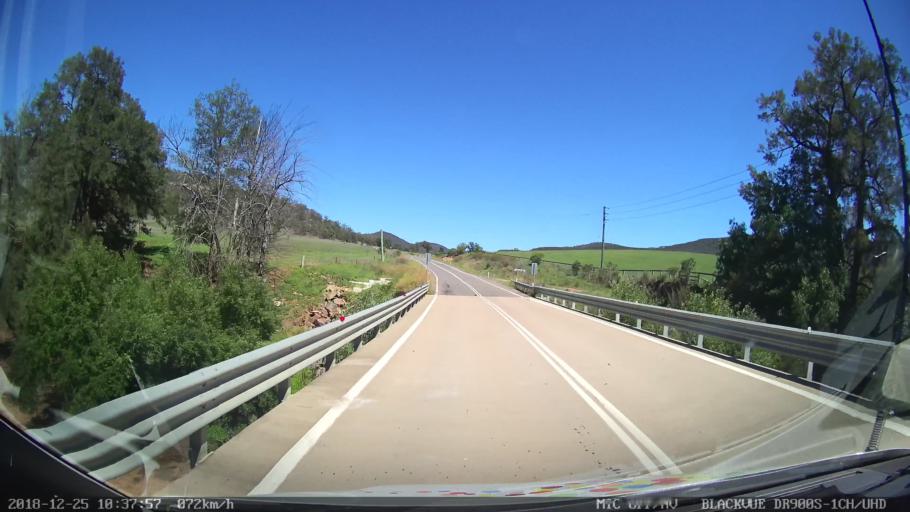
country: AU
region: New South Wales
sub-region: Upper Hunter Shire
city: Merriwa
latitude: -32.4059
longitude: 150.3735
